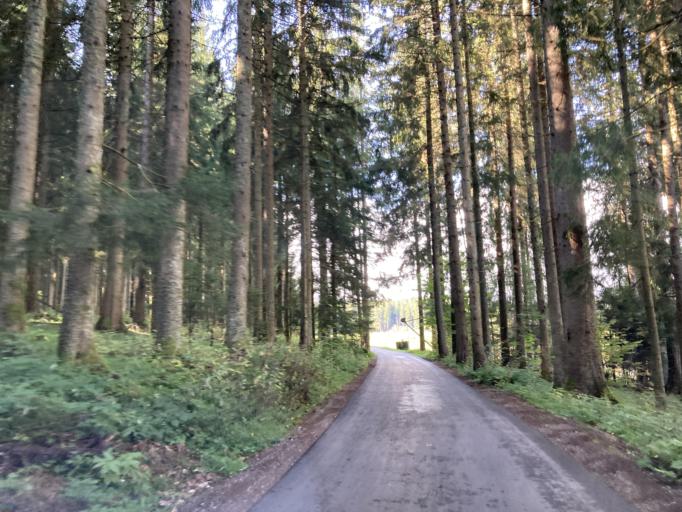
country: DE
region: Baden-Wuerttemberg
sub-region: Freiburg Region
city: Vohrenbach
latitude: 48.0956
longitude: 8.2815
